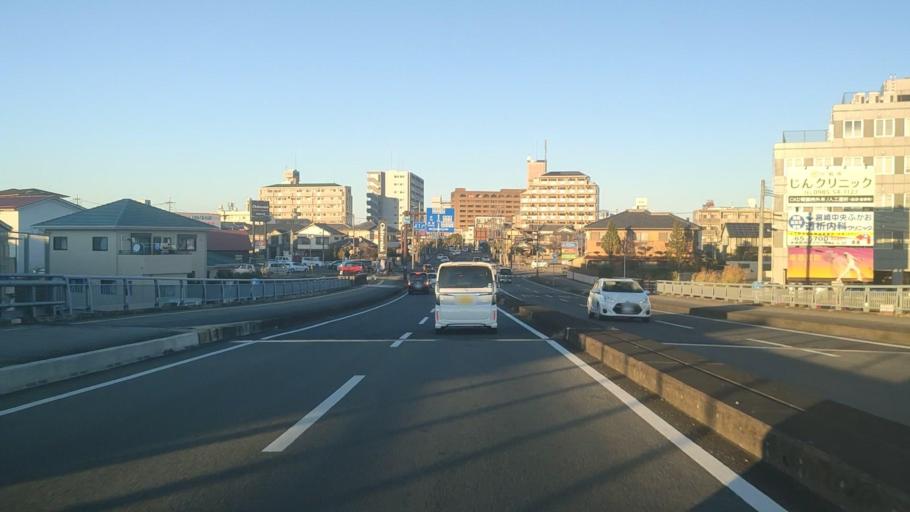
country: JP
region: Miyazaki
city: Miyazaki-shi
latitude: 31.9112
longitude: 131.4133
